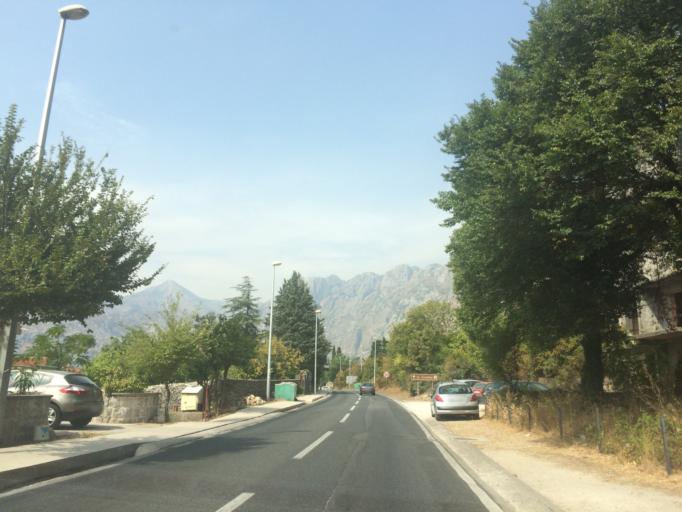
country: ME
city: Dobrota
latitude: 42.4616
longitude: 18.7651
